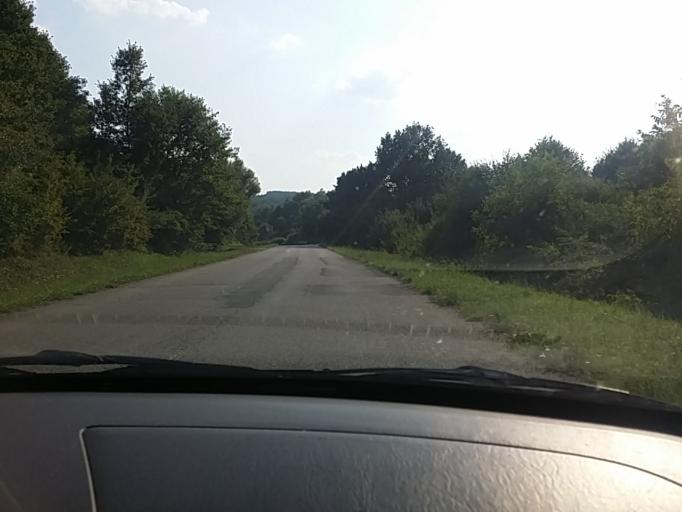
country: HU
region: Baranya
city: Sasd
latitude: 46.1681
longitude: 18.1345
